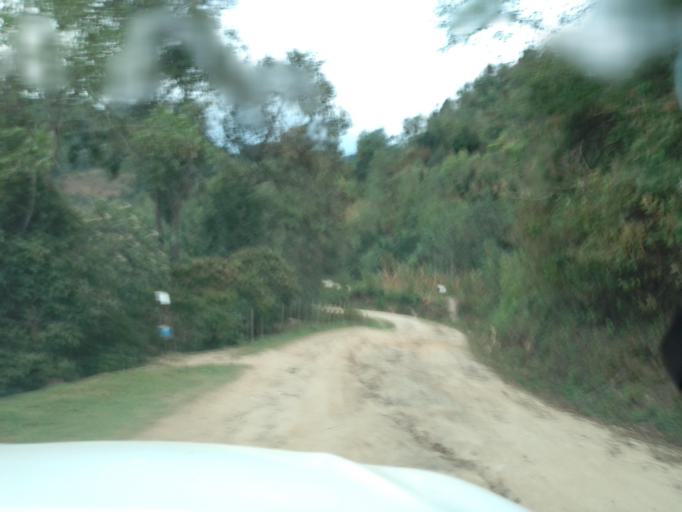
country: MX
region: Chiapas
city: Motozintla de Mendoza
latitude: 15.2158
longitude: -92.2293
